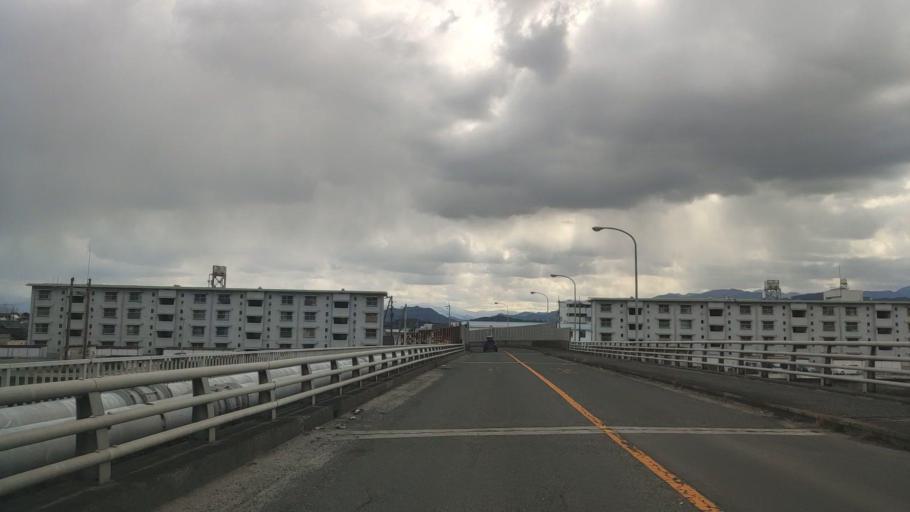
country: JP
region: Ehime
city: Saijo
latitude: 34.0594
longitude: 133.0175
